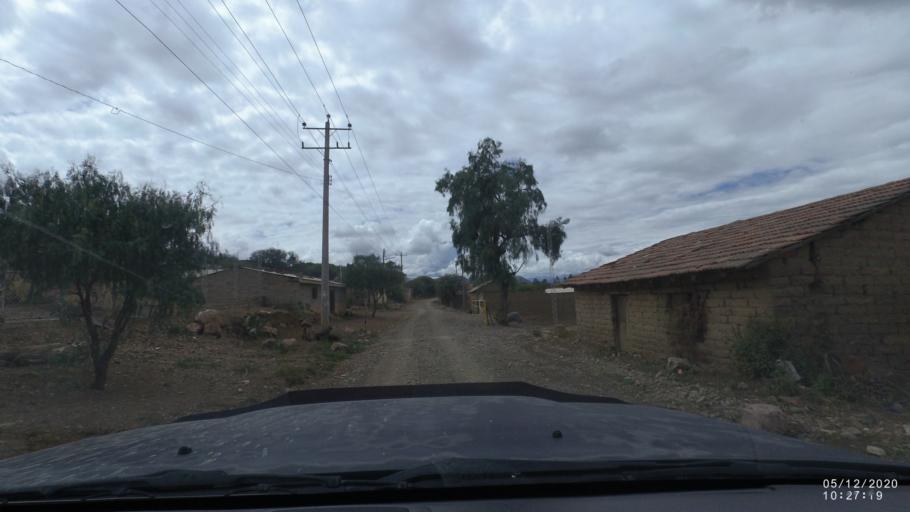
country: BO
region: Cochabamba
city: Sipe Sipe
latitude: -17.5321
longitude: -66.2790
